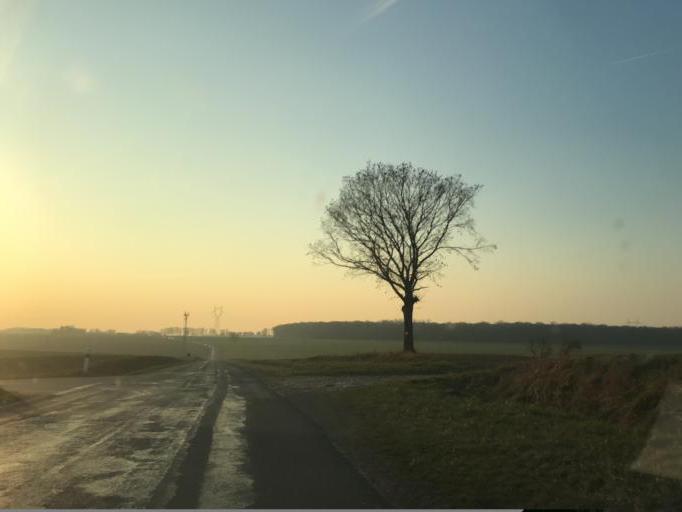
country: FR
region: Ile-de-France
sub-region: Departement de Seine-et-Marne
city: Juilly
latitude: 49.0161
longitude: 2.7341
